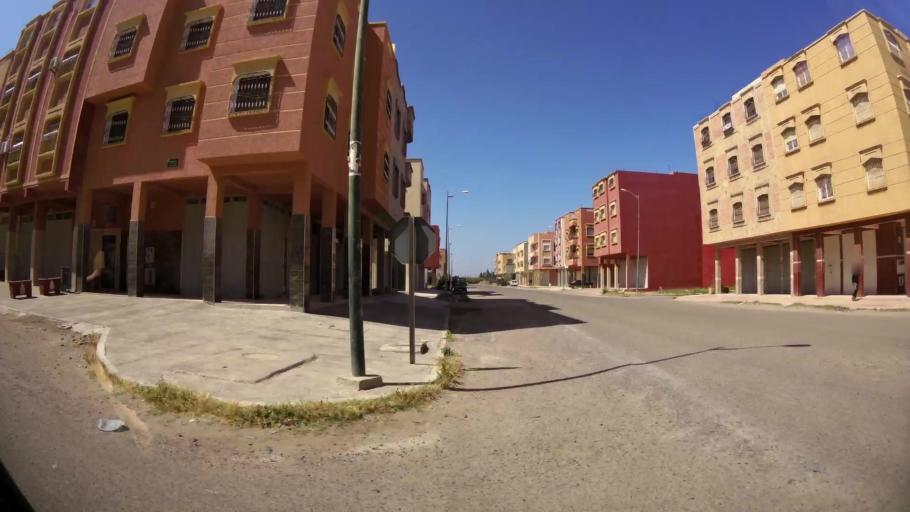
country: MA
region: Souss-Massa-Draa
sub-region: Inezgane-Ait Mellou
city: Inezgane
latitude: 30.3312
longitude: -9.5086
